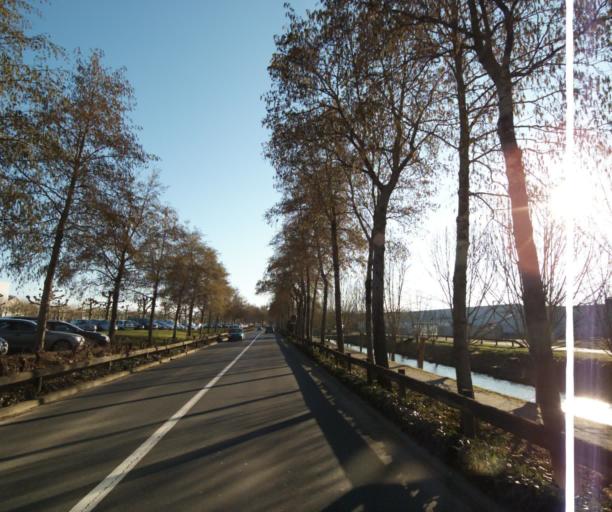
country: FR
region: Poitou-Charentes
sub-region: Departement des Deux-Sevres
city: Niort
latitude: 46.3303
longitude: -0.4888
